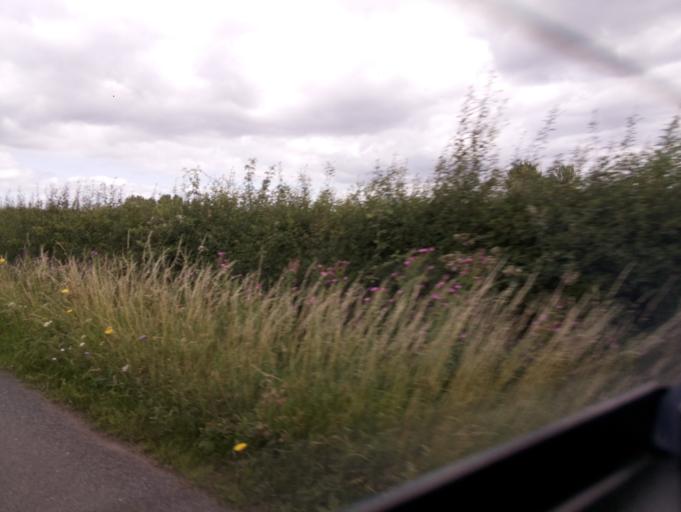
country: GB
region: England
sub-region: Milton Keynes
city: Shenley Church End
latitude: 51.9820
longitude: -0.8263
